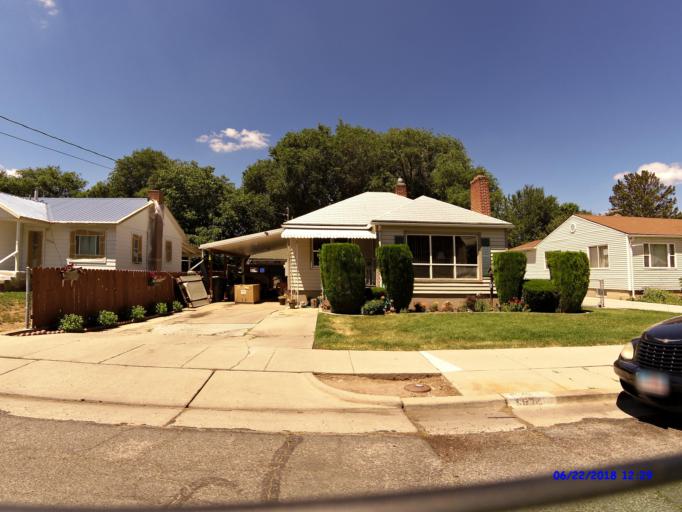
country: US
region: Utah
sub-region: Weber County
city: Ogden
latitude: 41.2390
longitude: -111.9604
